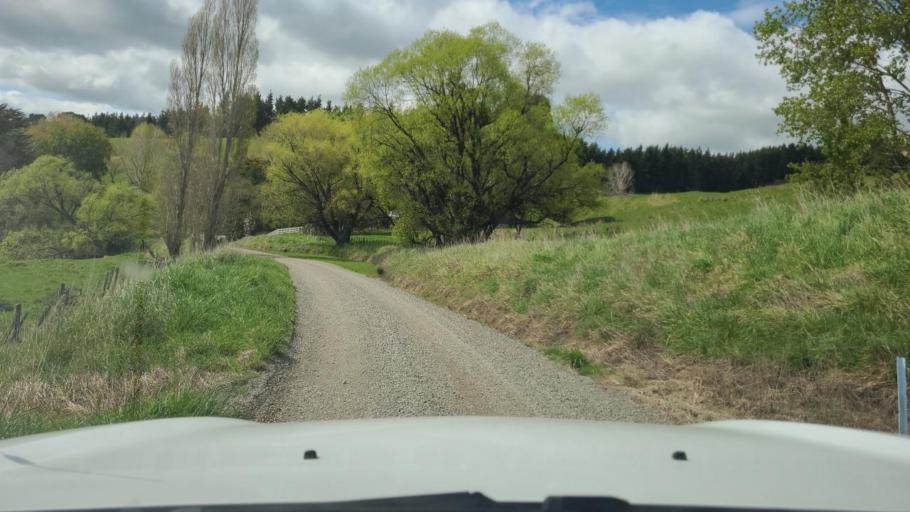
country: NZ
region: Wellington
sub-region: South Wairarapa District
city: Waipawa
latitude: -41.2167
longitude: 175.5820
